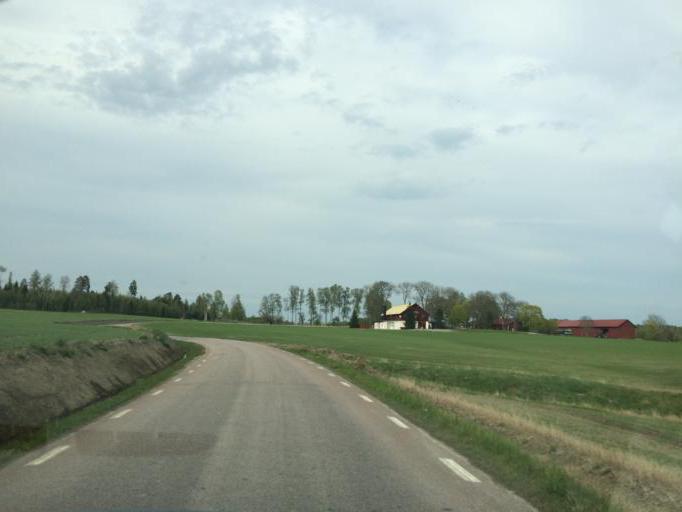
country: SE
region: Vaestmanland
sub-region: Kopings Kommun
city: Koping
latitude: 59.5940
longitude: 15.9964
